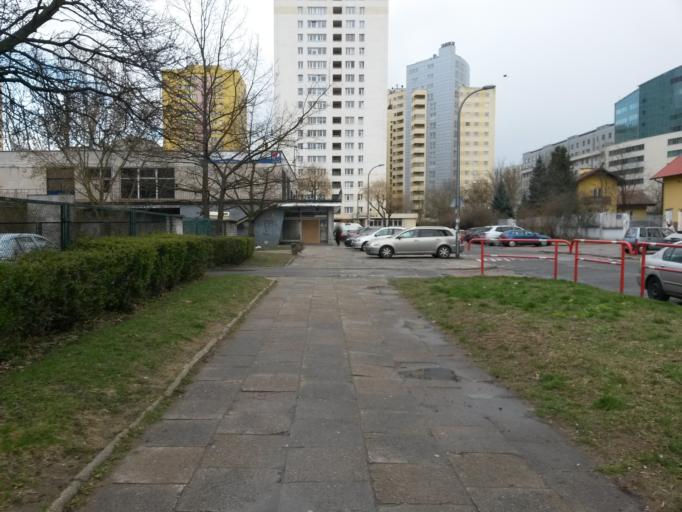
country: PL
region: Masovian Voivodeship
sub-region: Warszawa
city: Mokotow
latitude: 52.1837
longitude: 21.0268
